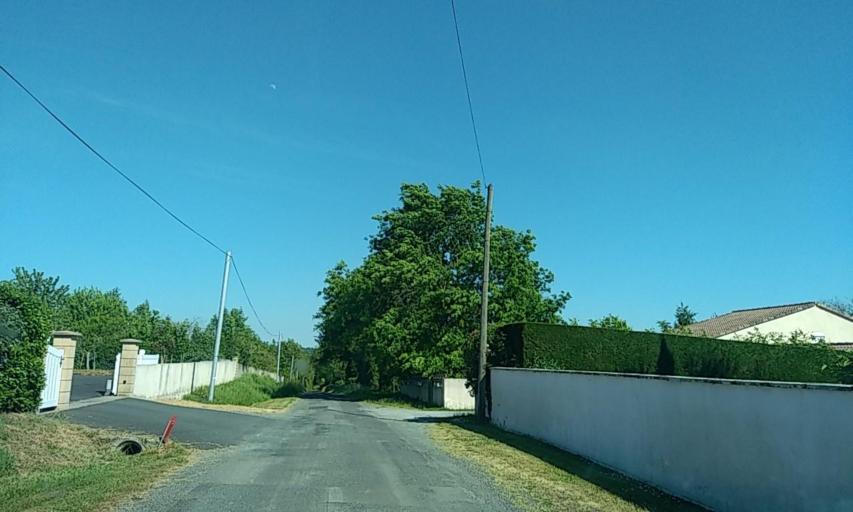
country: FR
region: Poitou-Charentes
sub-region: Departement des Deux-Sevres
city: Boisme
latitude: 46.7748
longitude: -0.4299
